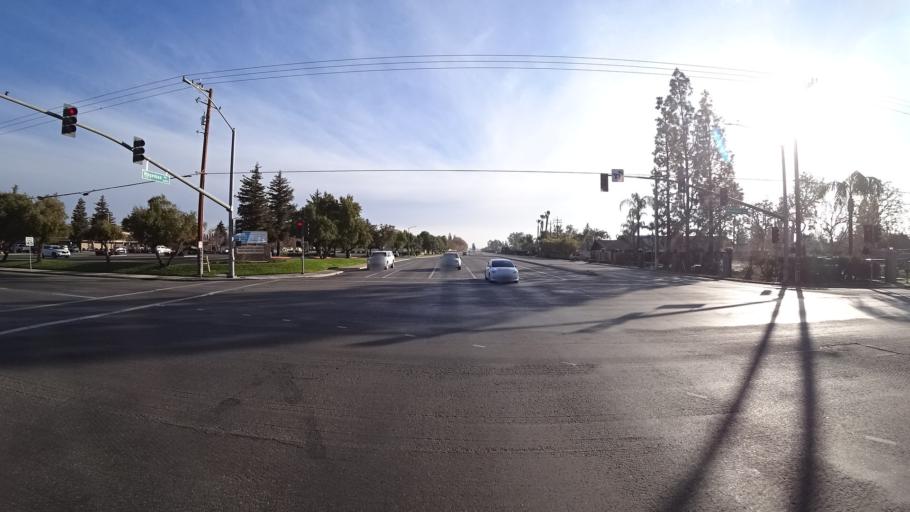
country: US
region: California
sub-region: Kern County
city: Greenacres
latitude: 35.4016
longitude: -119.0744
